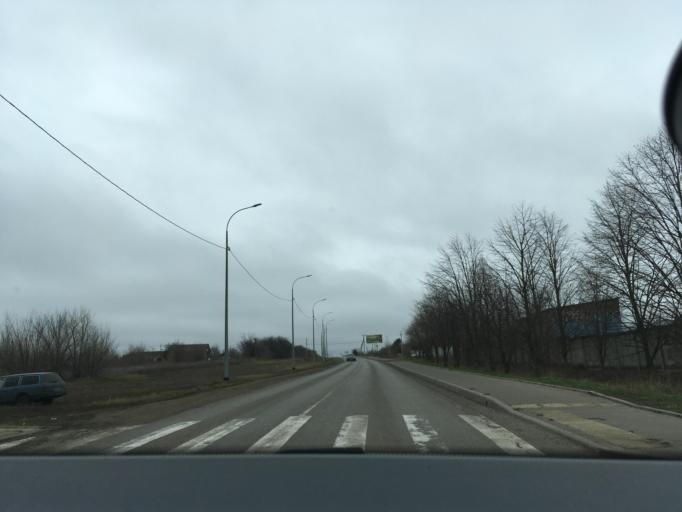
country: RU
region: Krasnodarskiy
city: Kushchevskaya
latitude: 46.5785
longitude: 39.6372
